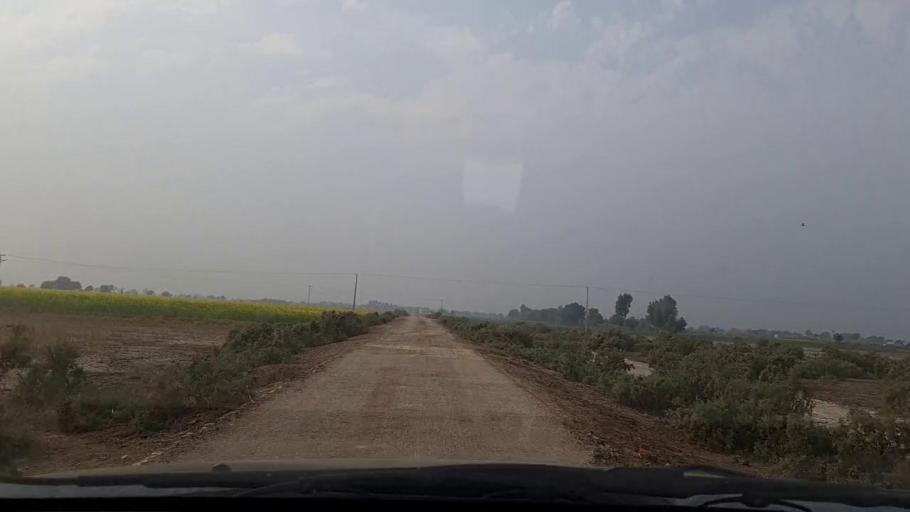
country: PK
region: Sindh
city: Pithoro
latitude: 25.7609
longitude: 69.3990
